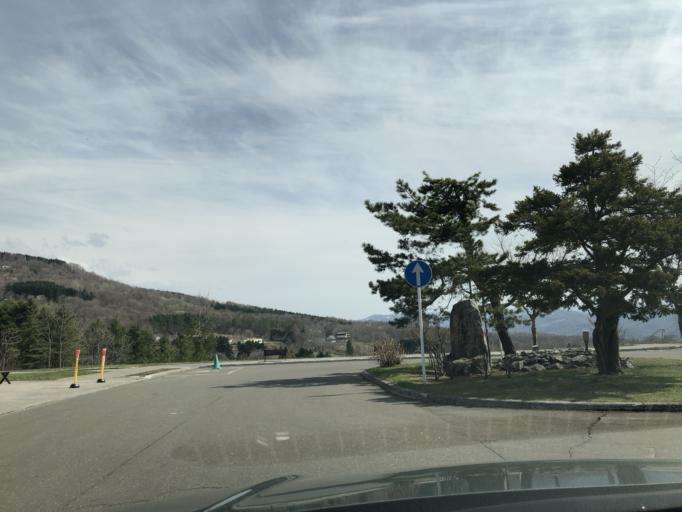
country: JP
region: Hokkaido
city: Akabira
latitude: 43.5964
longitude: 142.0471
